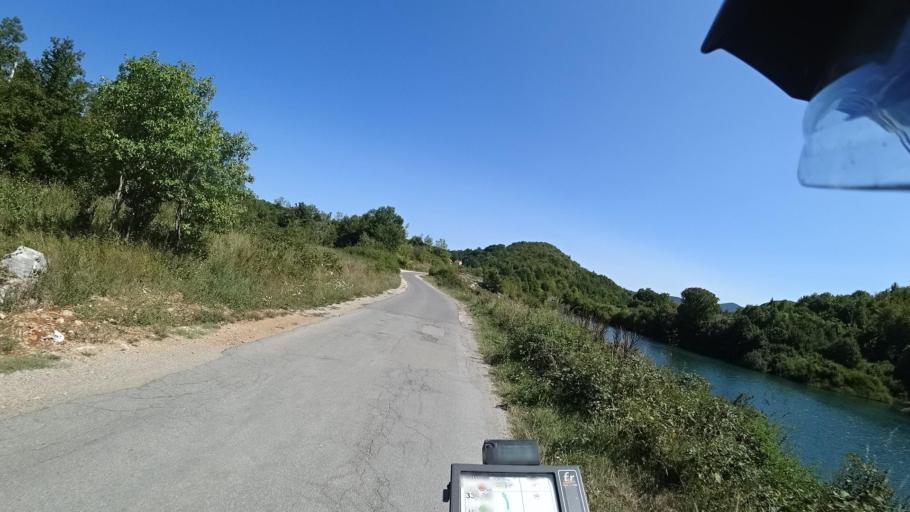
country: HR
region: Licko-Senjska
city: Popovaca
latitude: 44.7356
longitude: 15.2747
